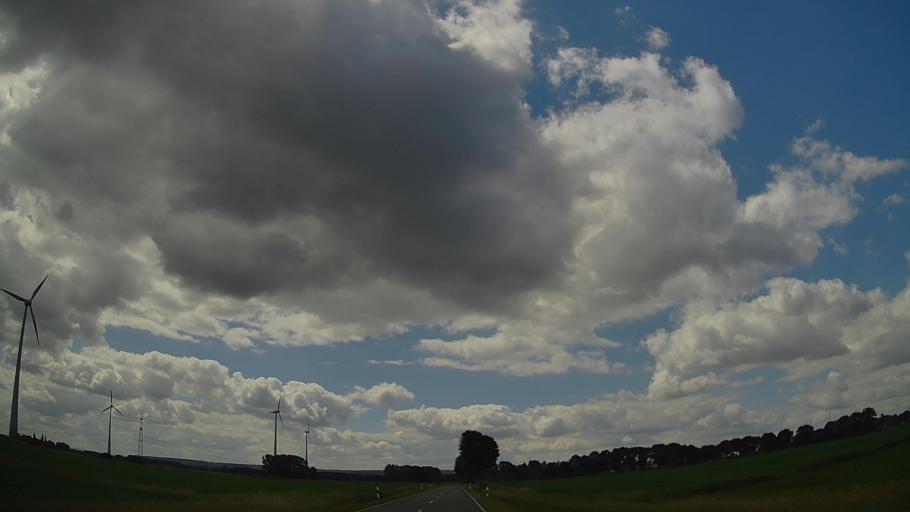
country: DE
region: Lower Saxony
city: Brockum
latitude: 52.5115
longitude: 8.4219
